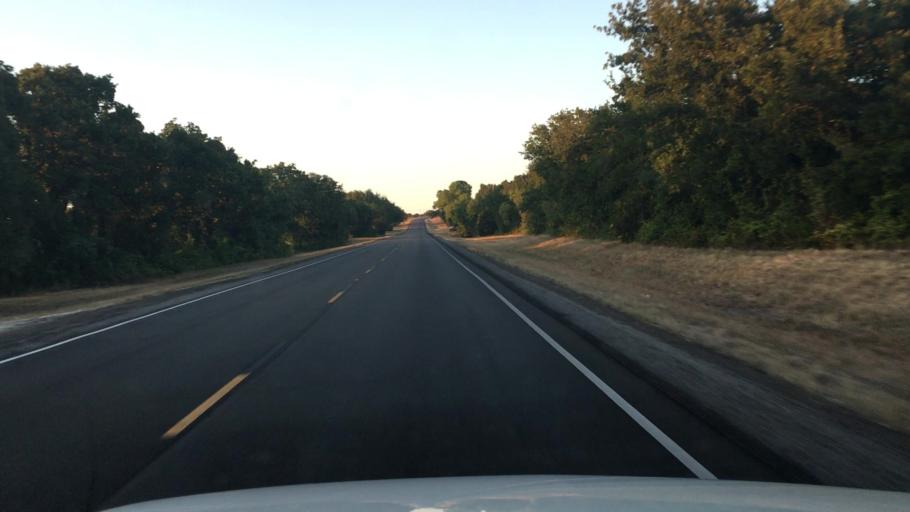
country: US
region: Texas
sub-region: Hamilton County
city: Hico
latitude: 32.0532
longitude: -97.9997
